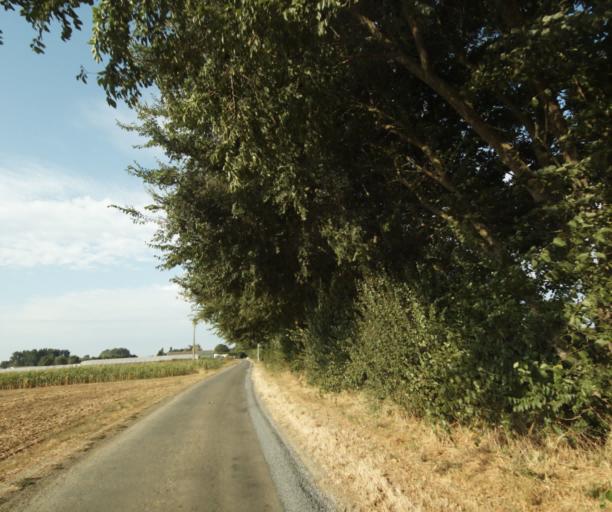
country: FR
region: Poitou-Charentes
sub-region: Departement de la Charente-Maritime
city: Cabariot
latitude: 45.9643
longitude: -0.8345
